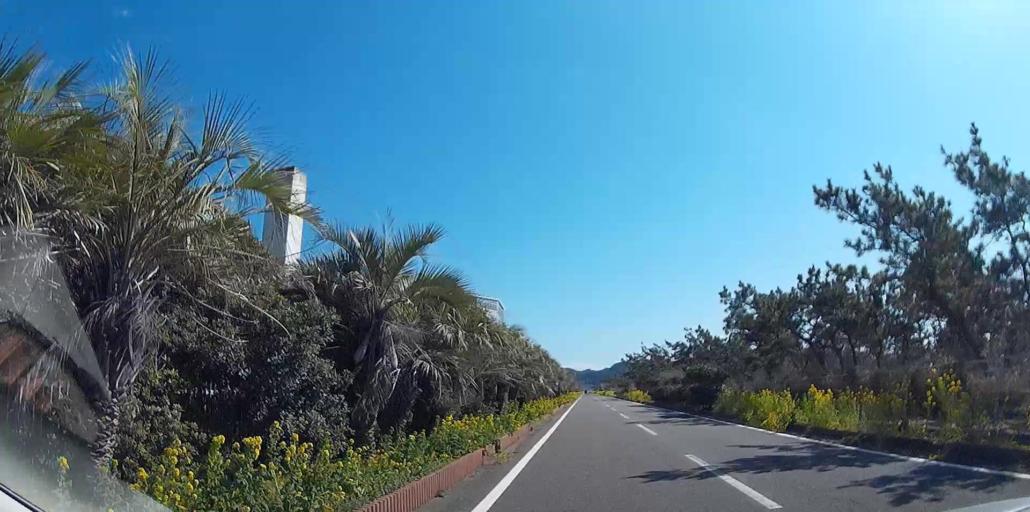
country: JP
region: Chiba
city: Tateyama
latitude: 34.9387
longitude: 139.8216
